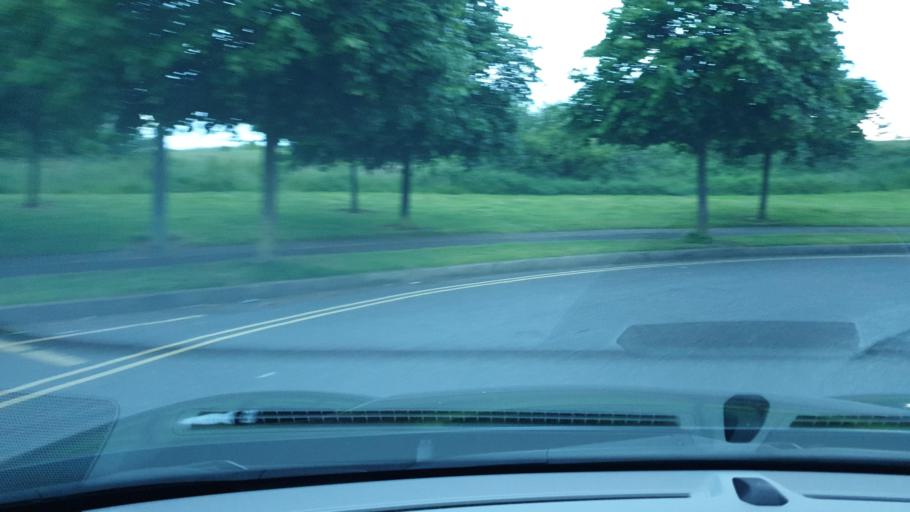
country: IE
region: Leinster
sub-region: Fingal County
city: Swords
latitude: 53.4475
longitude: -6.2179
